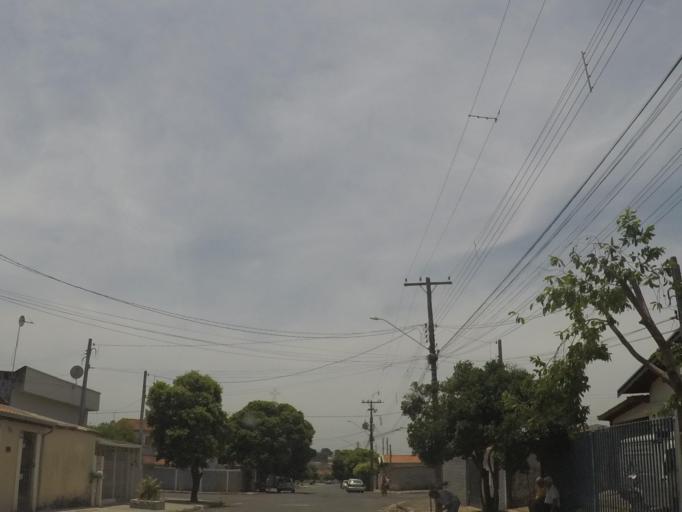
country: BR
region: Sao Paulo
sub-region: Hortolandia
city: Hortolandia
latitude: -22.8562
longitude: -47.1855
